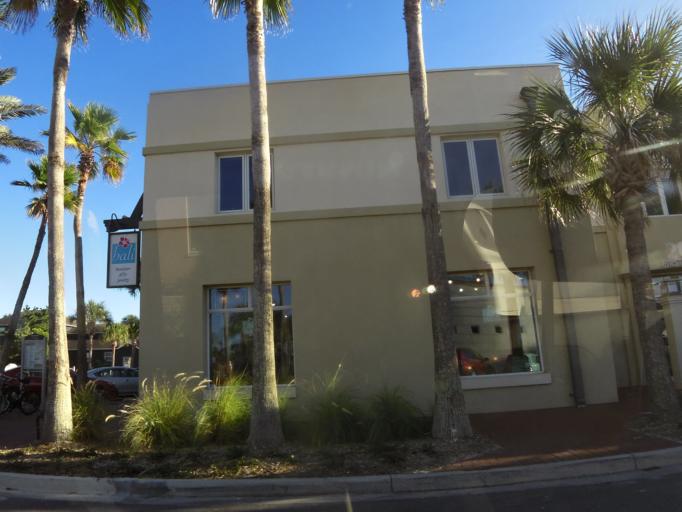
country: US
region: Florida
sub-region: Duval County
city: Atlantic Beach
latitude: 30.3237
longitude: -81.3961
